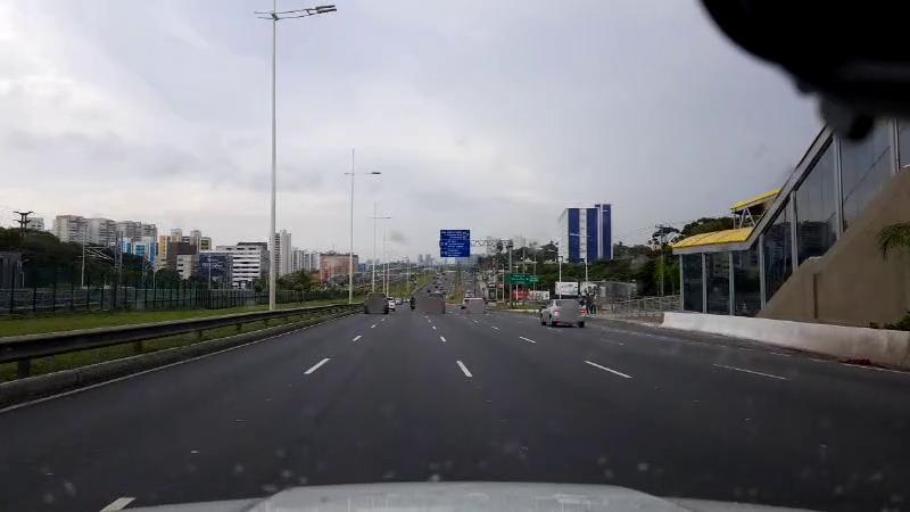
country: BR
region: Bahia
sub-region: Salvador
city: Salvador
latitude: -12.9563
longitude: -38.4298
